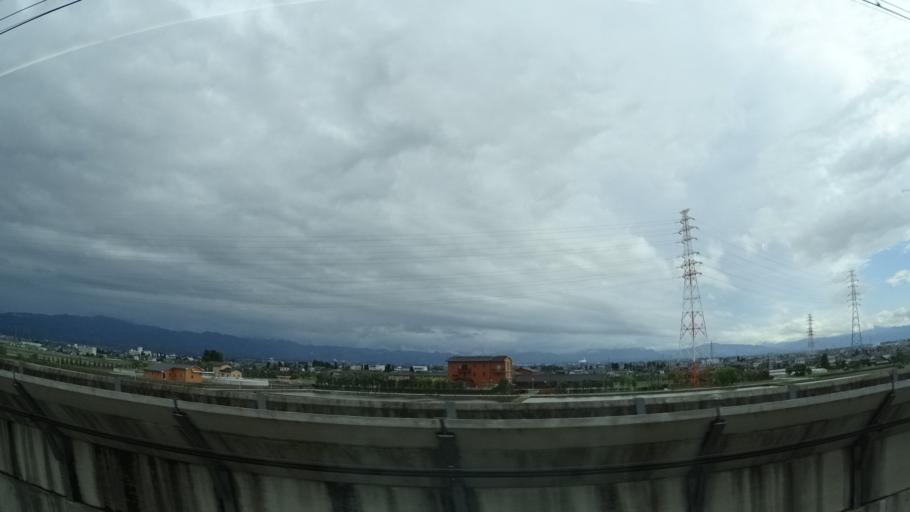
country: JP
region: Toyama
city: Namerikawa
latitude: 36.7125
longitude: 137.2995
